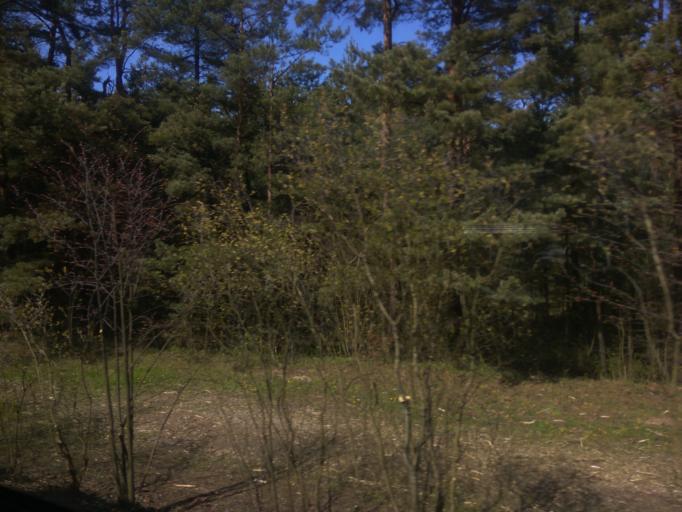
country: LV
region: Babite
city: Pinki
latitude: 56.9828
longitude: 23.8686
